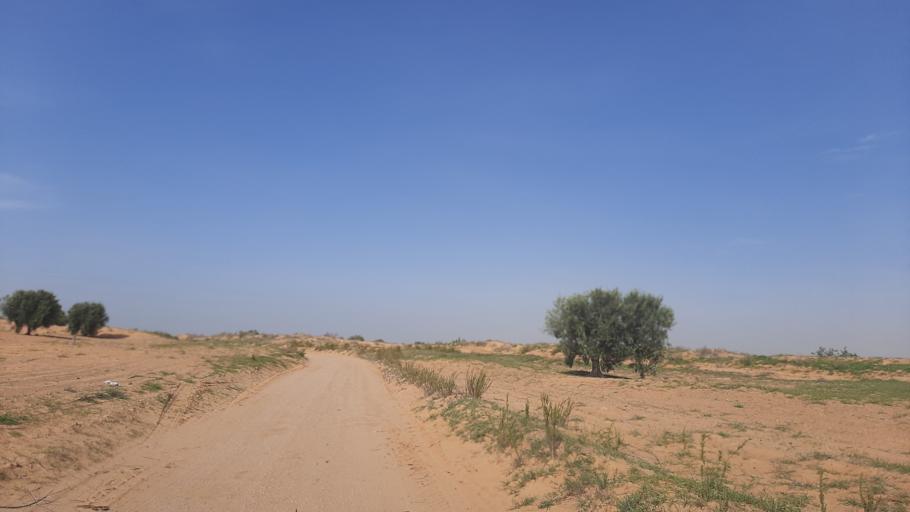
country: TN
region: Madanin
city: Zarzis
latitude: 33.4361
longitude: 10.8082
